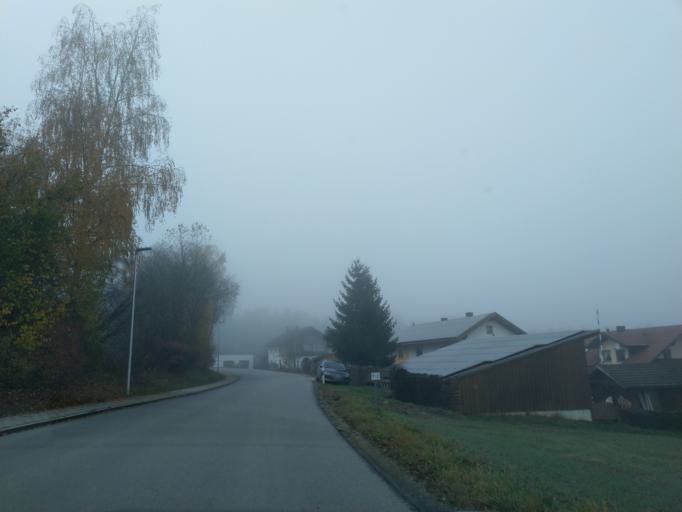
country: DE
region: Bavaria
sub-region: Lower Bavaria
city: Auerbach
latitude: 48.7812
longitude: 13.1124
